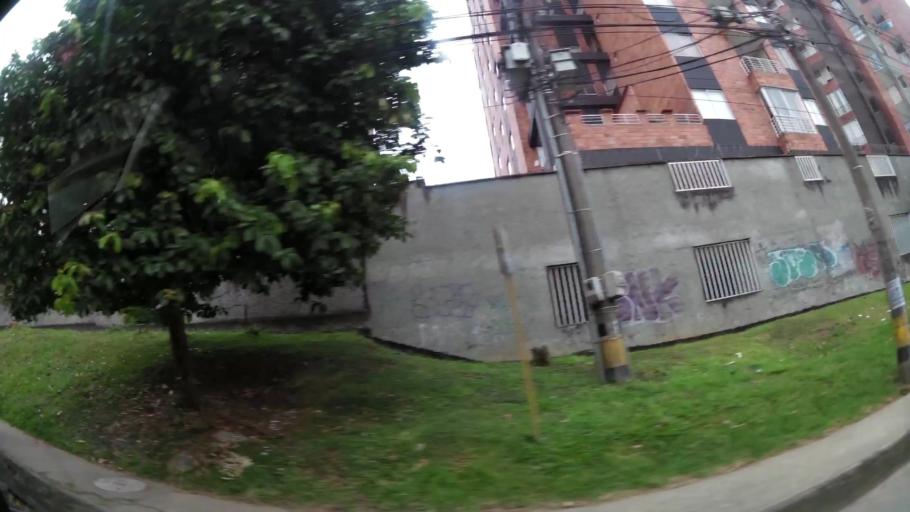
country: CO
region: Antioquia
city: Medellin
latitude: 6.2732
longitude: -75.5842
